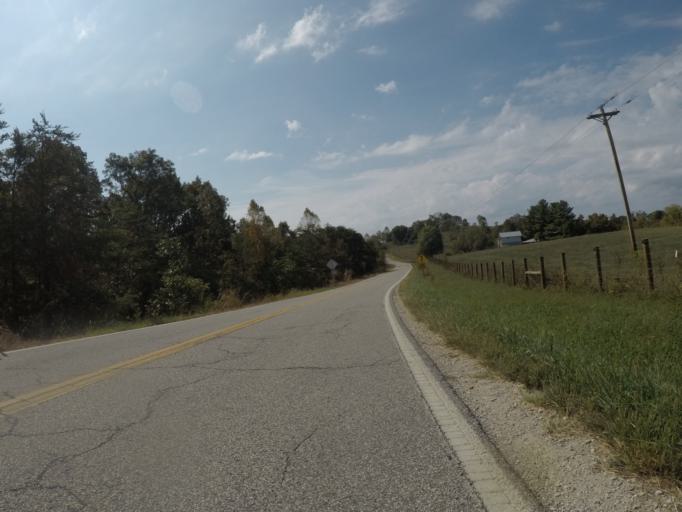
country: US
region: West Virginia
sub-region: Cabell County
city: Lesage
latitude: 38.5888
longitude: -82.4242
